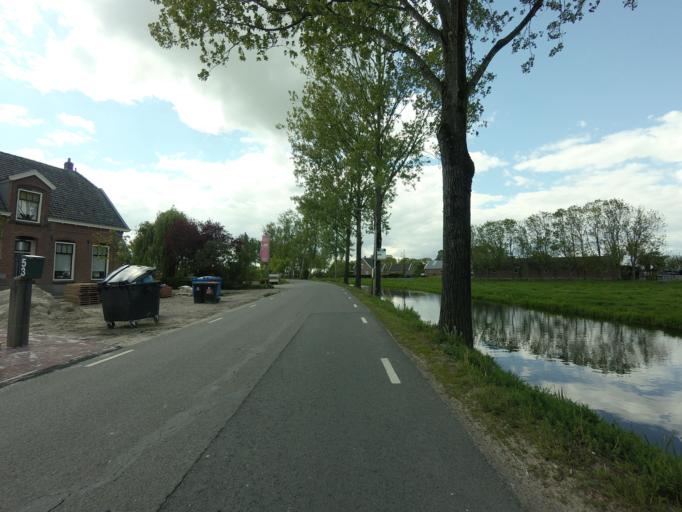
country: NL
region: South Holland
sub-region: Gemeente Leerdam
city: Leerdam
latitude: 51.9119
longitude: 5.0342
